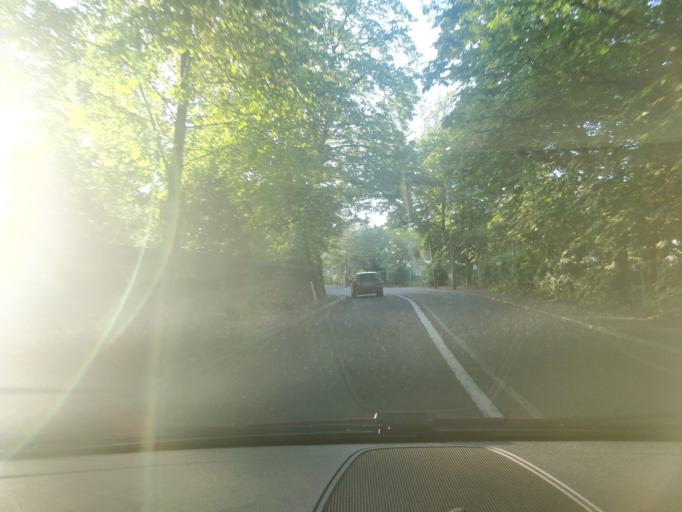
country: GB
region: England
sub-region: Lancashire
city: Parbold
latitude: 53.5923
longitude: -2.7640
